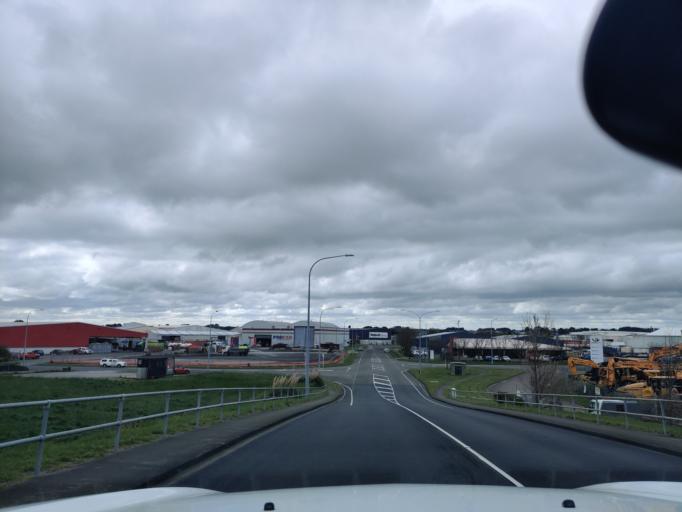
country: NZ
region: Manawatu-Wanganui
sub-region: Palmerston North City
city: Palmerston North
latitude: -40.3370
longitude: 175.6441
